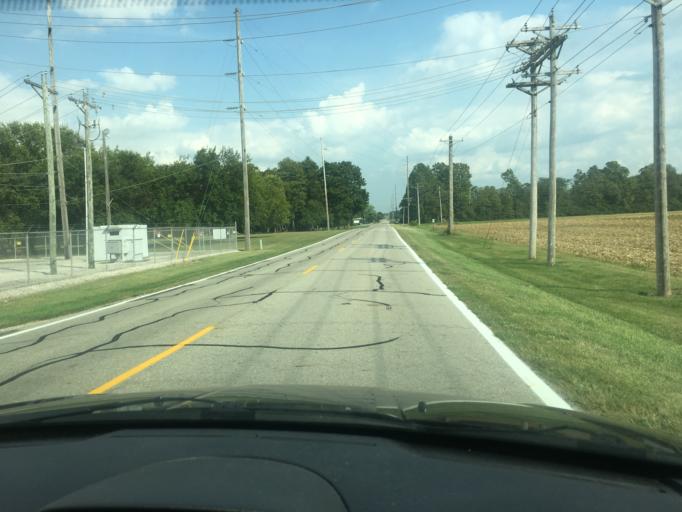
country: US
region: Ohio
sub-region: Champaign County
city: Urbana
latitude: 40.1302
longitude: -83.8130
